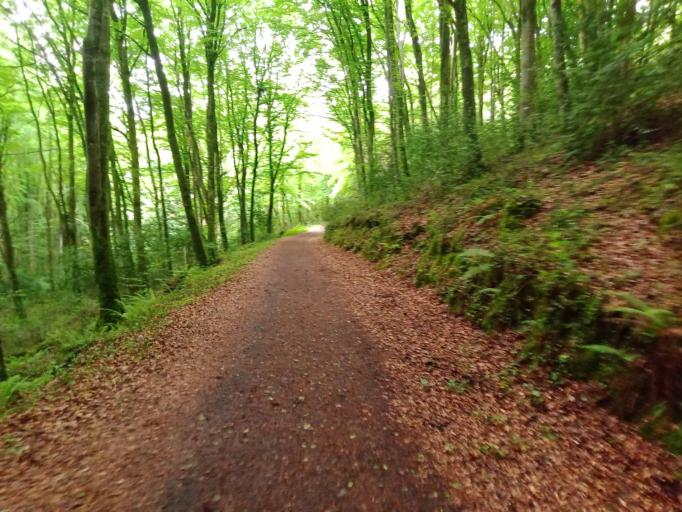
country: IE
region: Leinster
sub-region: Laois
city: Stradbally
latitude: 53.0008
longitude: -7.1181
